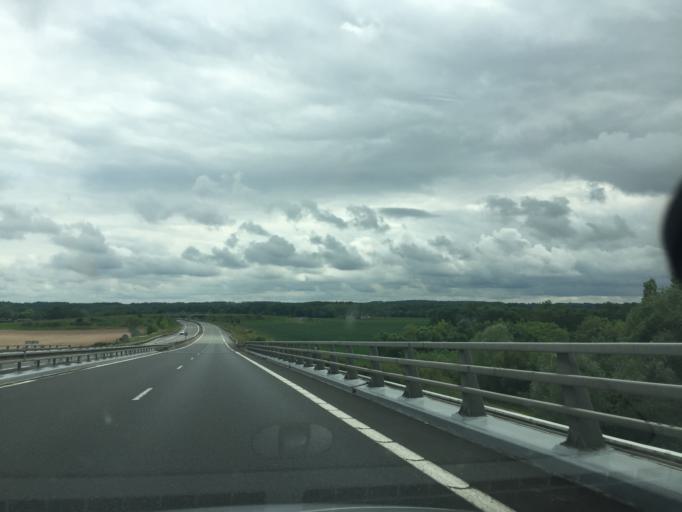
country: FR
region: Pays de la Loire
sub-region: Departement de la Sarthe
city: Luceau
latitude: 47.6751
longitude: 0.3719
